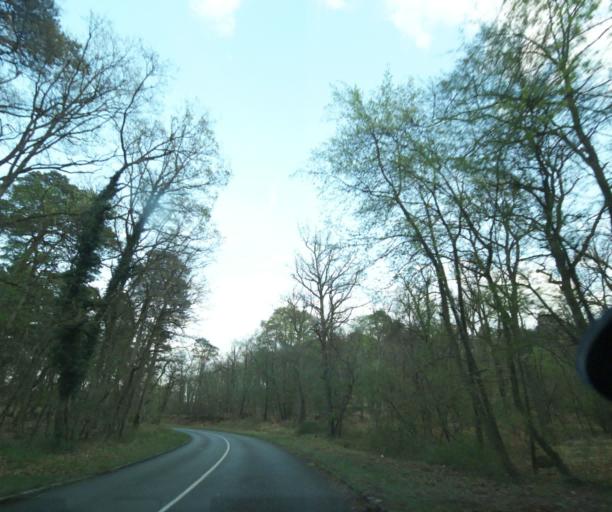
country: FR
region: Ile-de-France
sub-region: Departement de Seine-et-Marne
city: Fontainebleau
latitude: 48.3898
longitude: 2.7100
